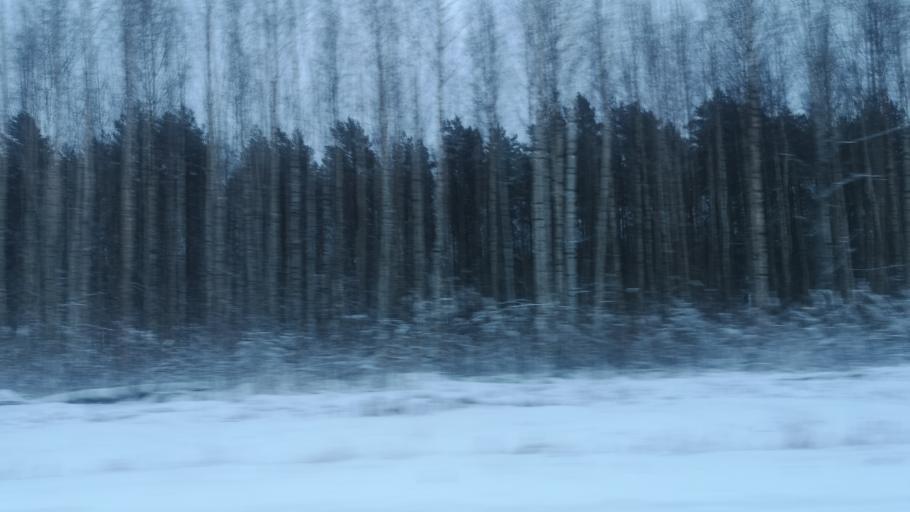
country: FI
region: Southern Savonia
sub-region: Savonlinna
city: Enonkoski
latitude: 62.0491
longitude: 28.7046
